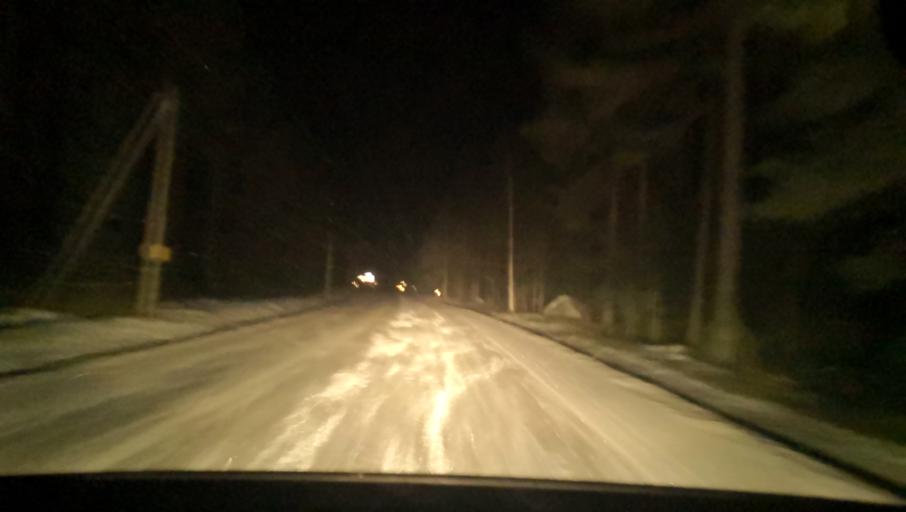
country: SE
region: Uppsala
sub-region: Heby Kommun
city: Tarnsjo
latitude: 60.1377
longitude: 16.9040
